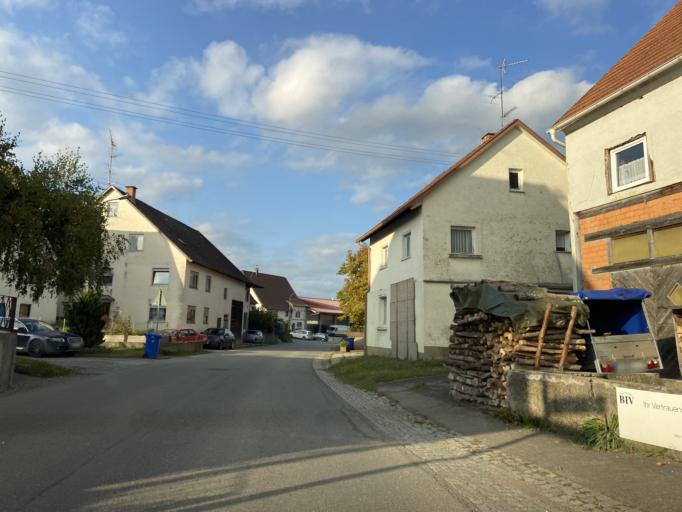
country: DE
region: Baden-Wuerttemberg
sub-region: Tuebingen Region
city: Scheer
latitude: 48.0929
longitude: 9.3299
